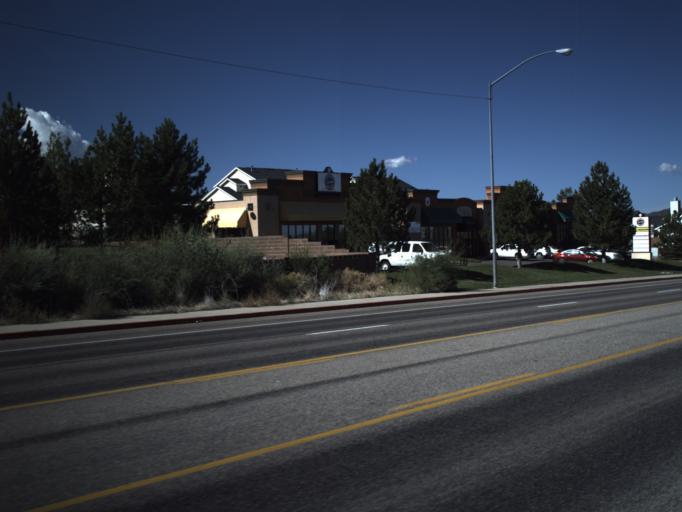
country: US
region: Utah
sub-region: Iron County
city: Cedar City
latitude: 37.6835
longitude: -113.0927
